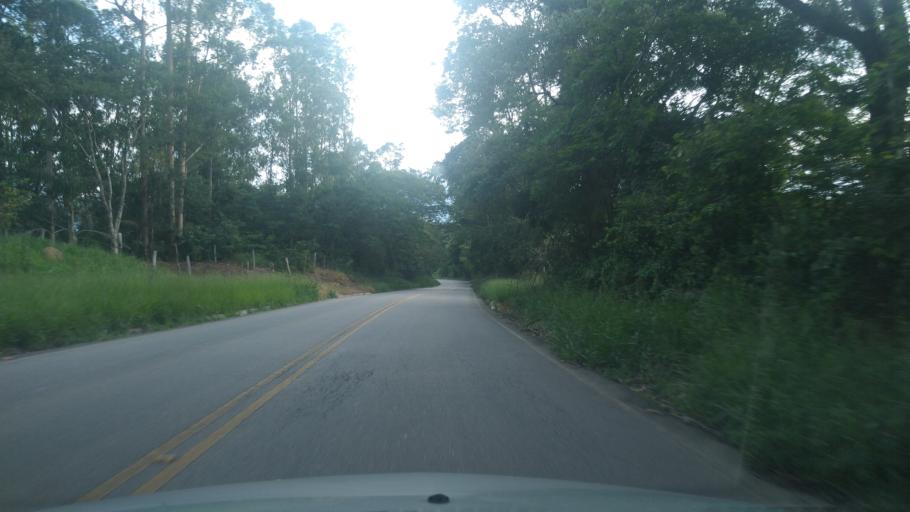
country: BR
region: Minas Gerais
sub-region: Extrema
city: Extrema
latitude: -22.7829
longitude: -46.3209
